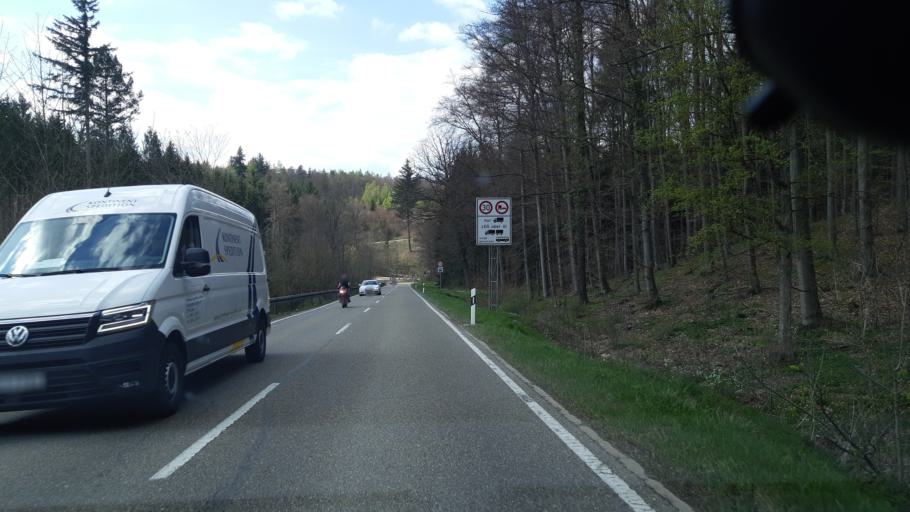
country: DE
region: Baden-Wuerttemberg
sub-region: Regierungsbezirk Stuttgart
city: Oberkochen
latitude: 48.8032
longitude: 10.1492
